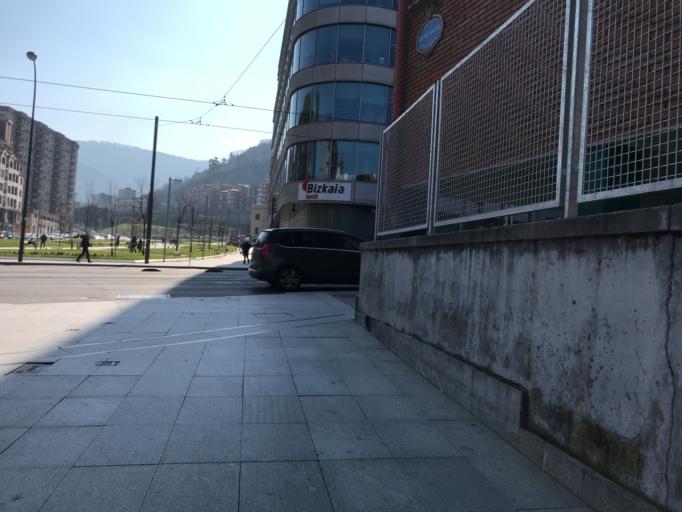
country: ES
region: Basque Country
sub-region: Bizkaia
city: Bilbao
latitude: 43.2582
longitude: -2.9485
